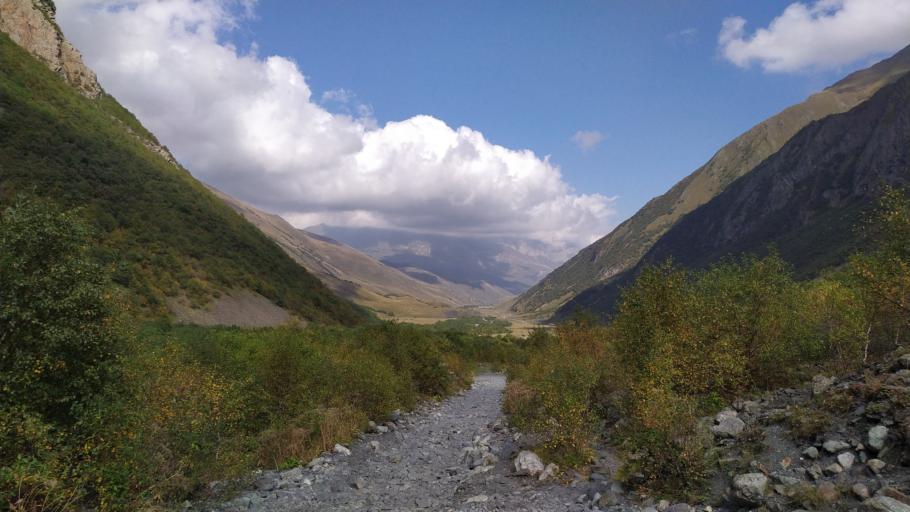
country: RU
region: North Ossetia
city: Verkhniy Fiagdon
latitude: 42.7708
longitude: 44.3640
